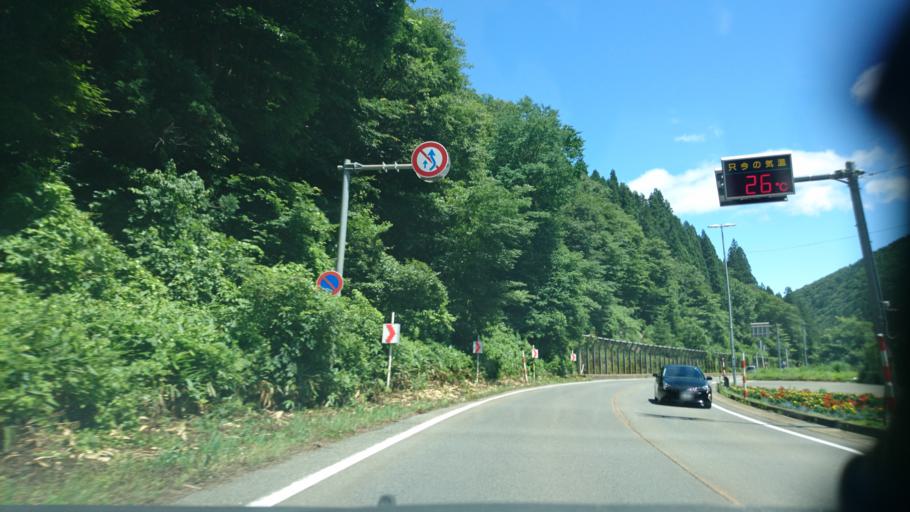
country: JP
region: Akita
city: Kakunodatemachi
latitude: 39.6425
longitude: 140.6605
